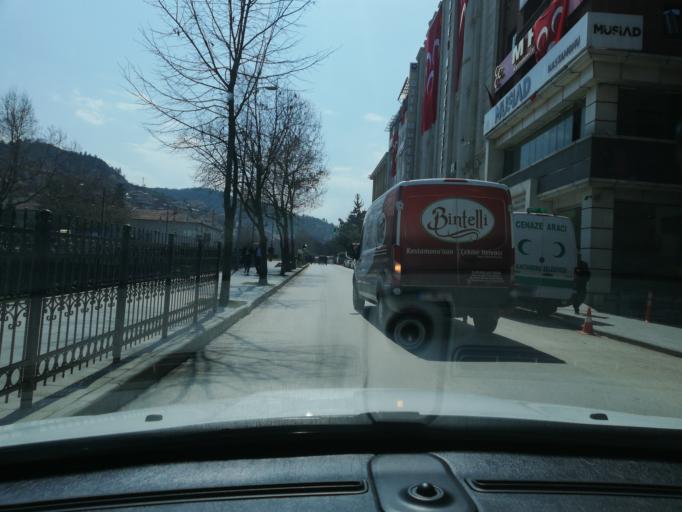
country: TR
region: Kastamonu
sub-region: Cide
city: Kastamonu
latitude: 41.3776
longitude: 33.7763
